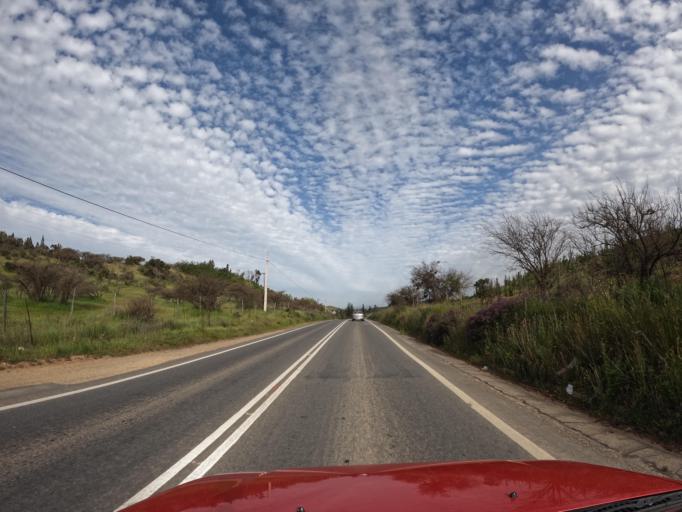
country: CL
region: O'Higgins
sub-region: Provincia de Colchagua
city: Santa Cruz
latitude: -34.3137
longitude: -71.7719
